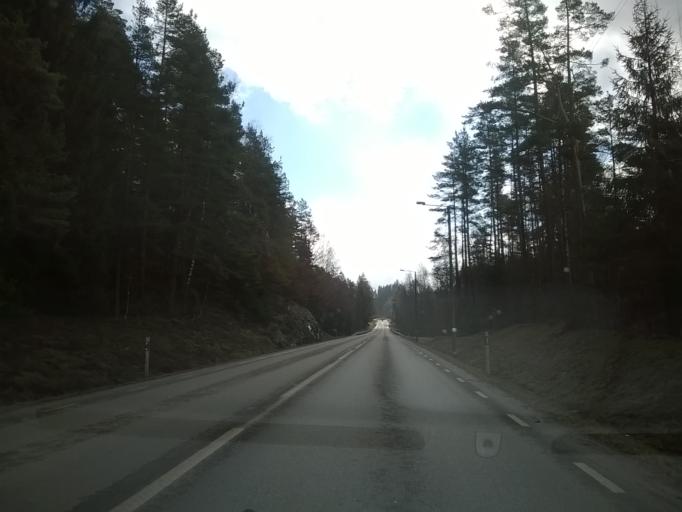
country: SE
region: Vaestra Goetaland
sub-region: Marks Kommun
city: Horred
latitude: 57.1426
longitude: 12.6940
